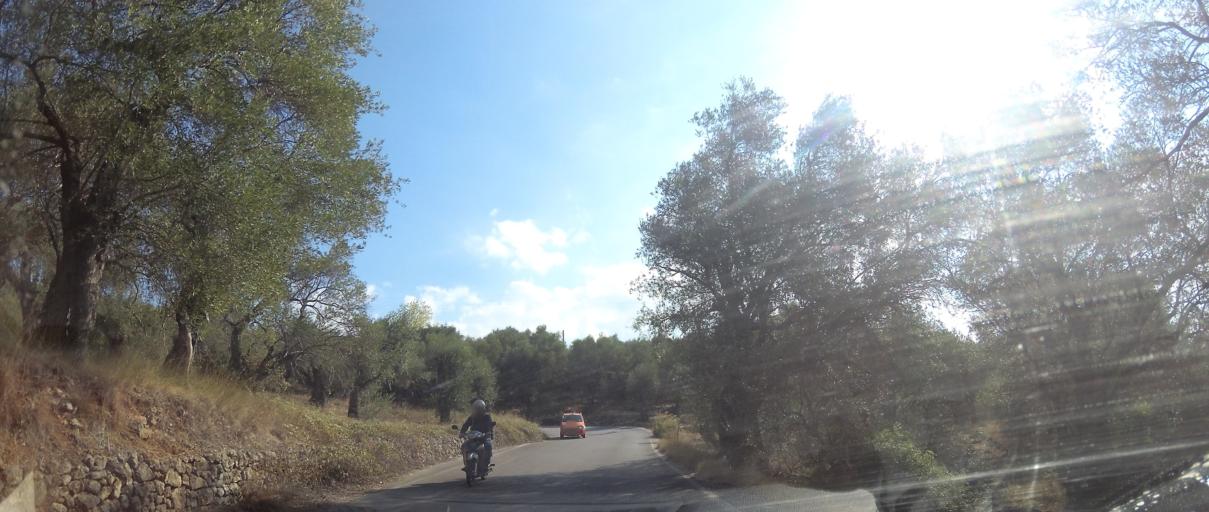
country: GR
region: Ionian Islands
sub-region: Nomos Kerkyras
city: Kontokali
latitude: 39.7115
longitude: 19.8456
